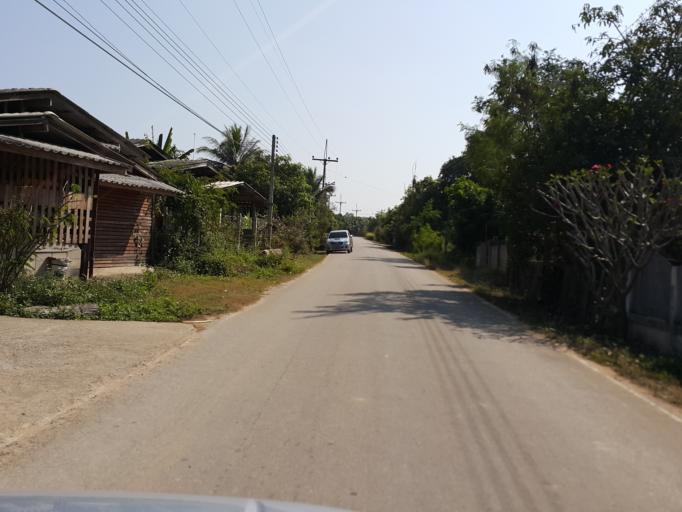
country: TH
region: Lampang
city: Wang Nuea
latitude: 19.0470
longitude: 99.6232
